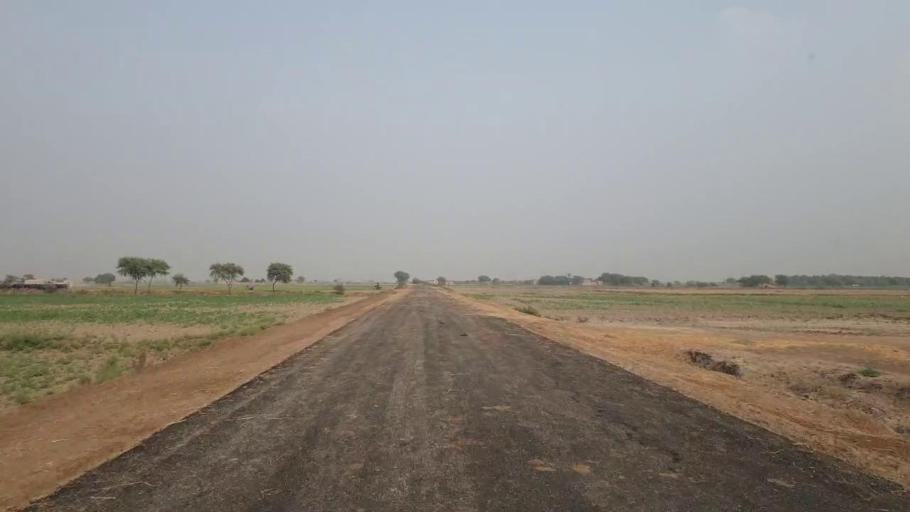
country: PK
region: Sindh
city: Mirpur Batoro
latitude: 24.5905
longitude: 68.4021
